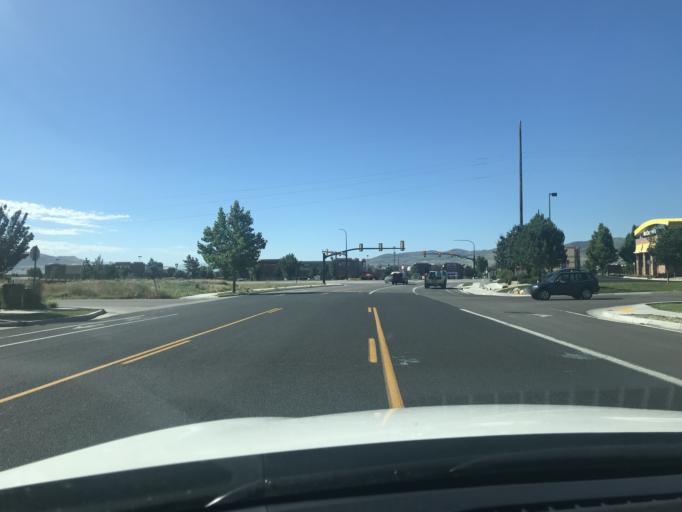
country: US
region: Utah
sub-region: Salt Lake County
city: South Jordan Heights
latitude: 40.5453
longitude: -111.9817
